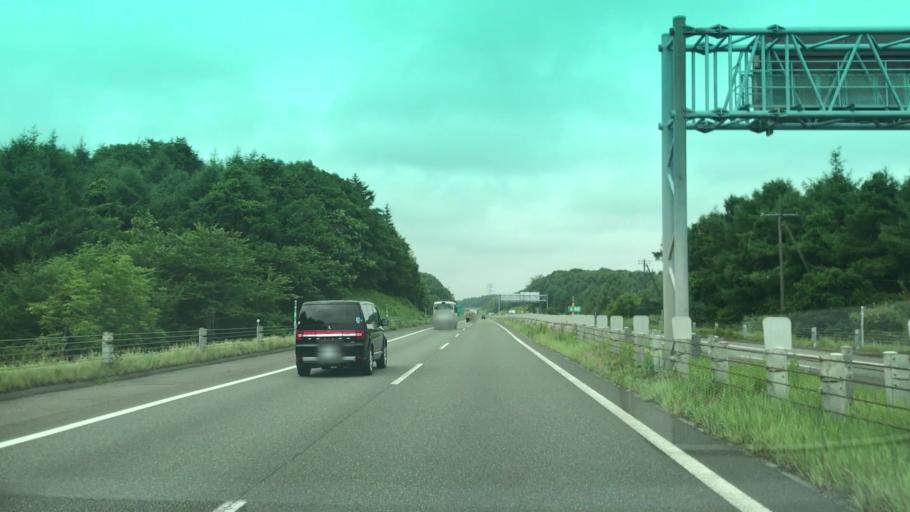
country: JP
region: Hokkaido
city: Tomakomai
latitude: 42.7203
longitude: 141.6527
